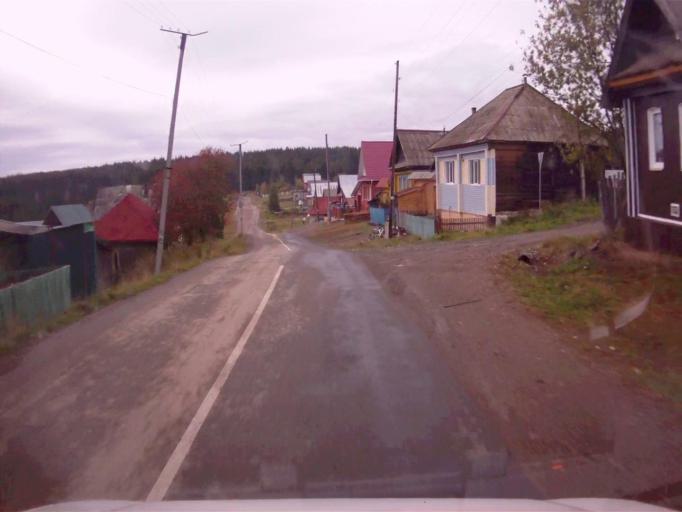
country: RU
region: Chelyabinsk
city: Nyazepetrovsk
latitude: 56.0628
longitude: 59.5736
